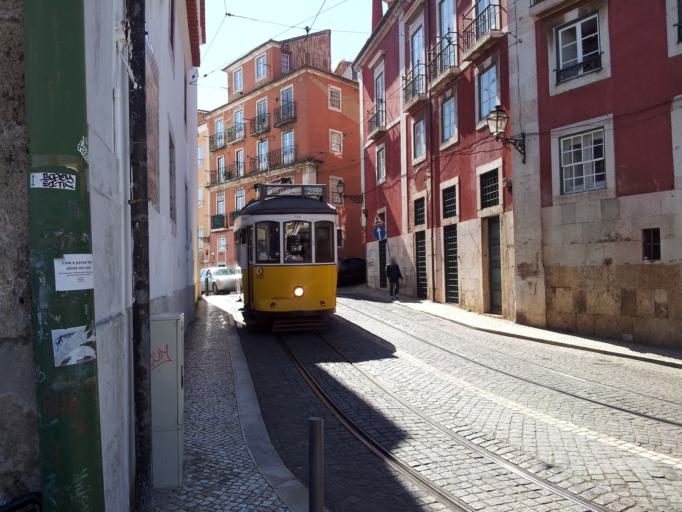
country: PT
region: Lisbon
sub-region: Lisbon
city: Lisbon
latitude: 38.7121
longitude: -9.1303
